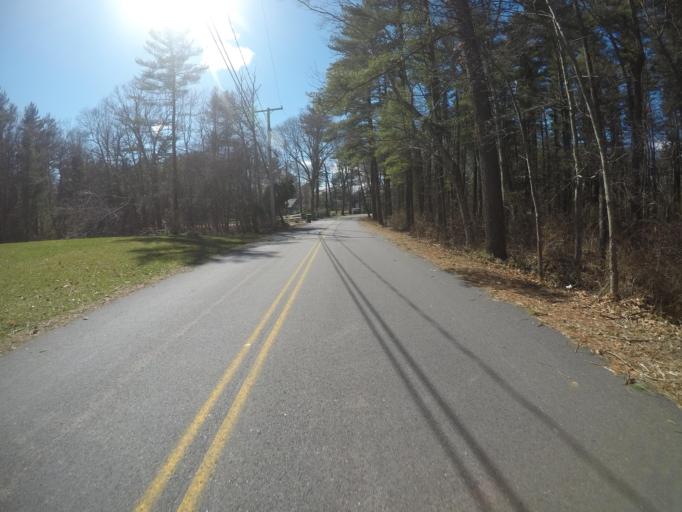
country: US
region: Massachusetts
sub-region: Bristol County
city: Easton
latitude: 41.9977
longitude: -71.1137
